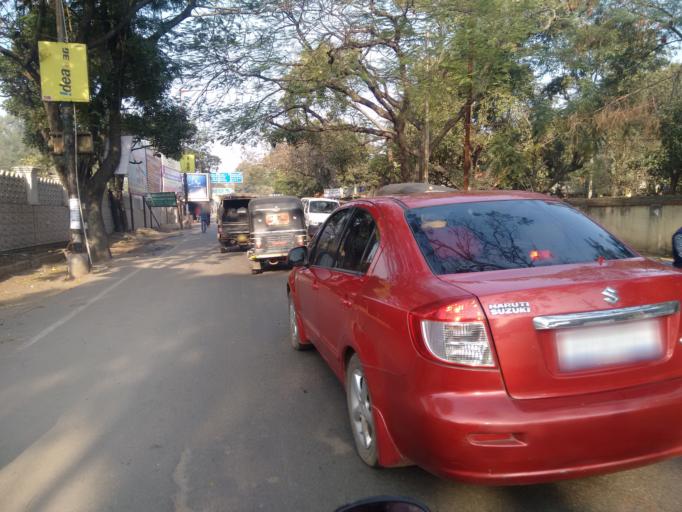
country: IN
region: Jharkhand
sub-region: Ranchi
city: Ranchi
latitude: 23.3772
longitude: 85.3307
